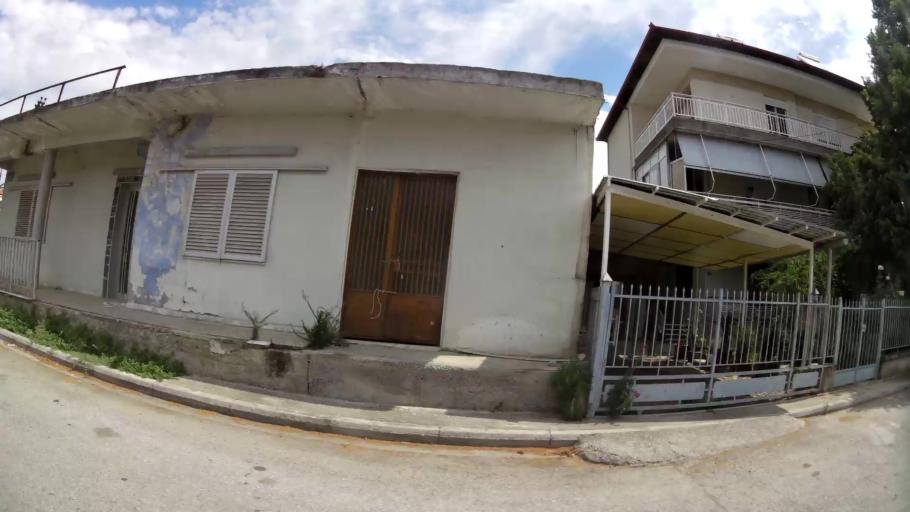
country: GR
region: Central Macedonia
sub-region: Nomos Pierias
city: Katerini
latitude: 40.2791
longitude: 22.4964
